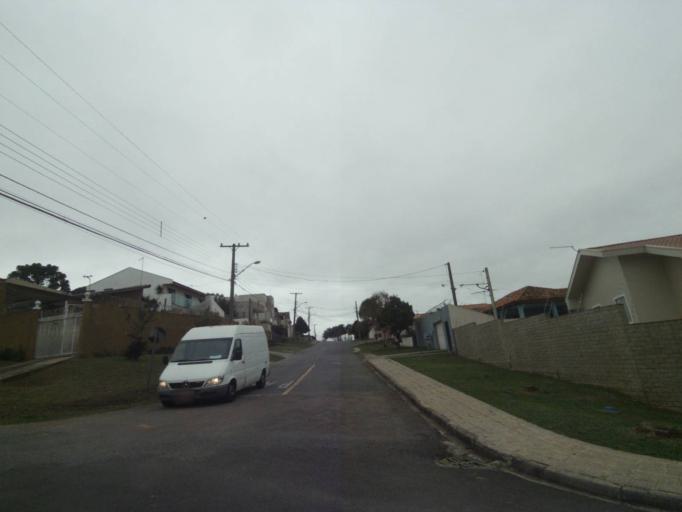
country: BR
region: Parana
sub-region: Curitiba
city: Curitiba
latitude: -25.4682
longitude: -49.2770
